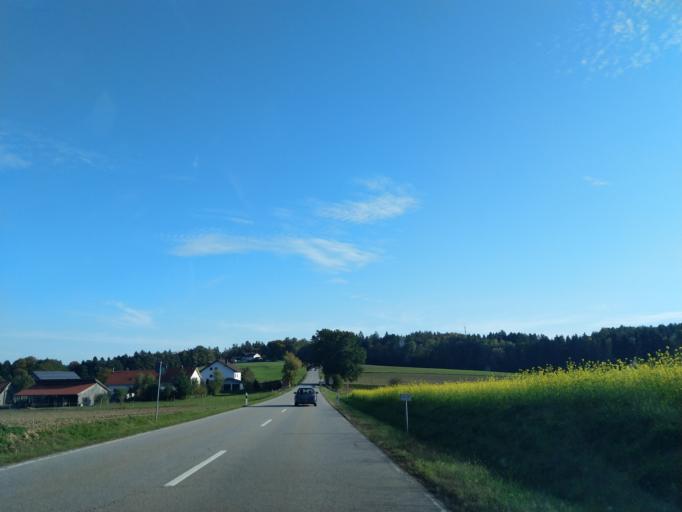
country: DE
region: Bavaria
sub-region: Lower Bavaria
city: Metten
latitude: 48.8583
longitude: 12.9409
